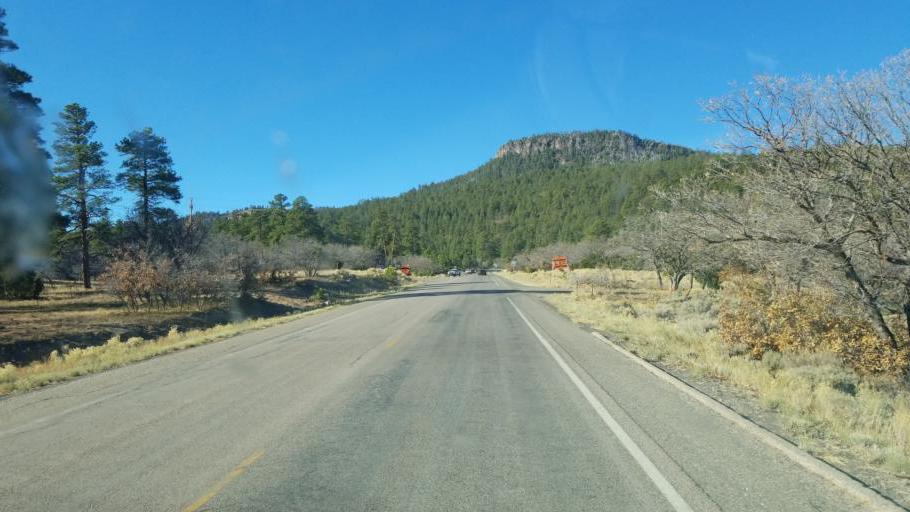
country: US
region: New Mexico
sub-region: McKinley County
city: Navajo
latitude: 36.0963
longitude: -108.8349
